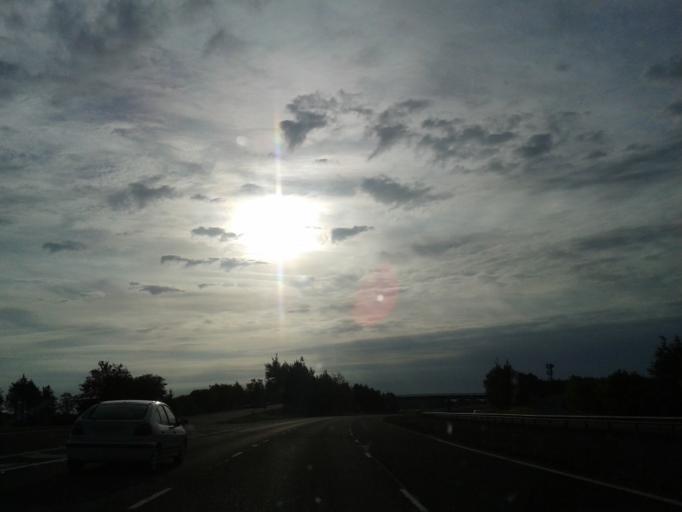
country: GB
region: Scotland
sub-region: Dumfries and Galloway
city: Gretna
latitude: 55.0270
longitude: -3.1324
